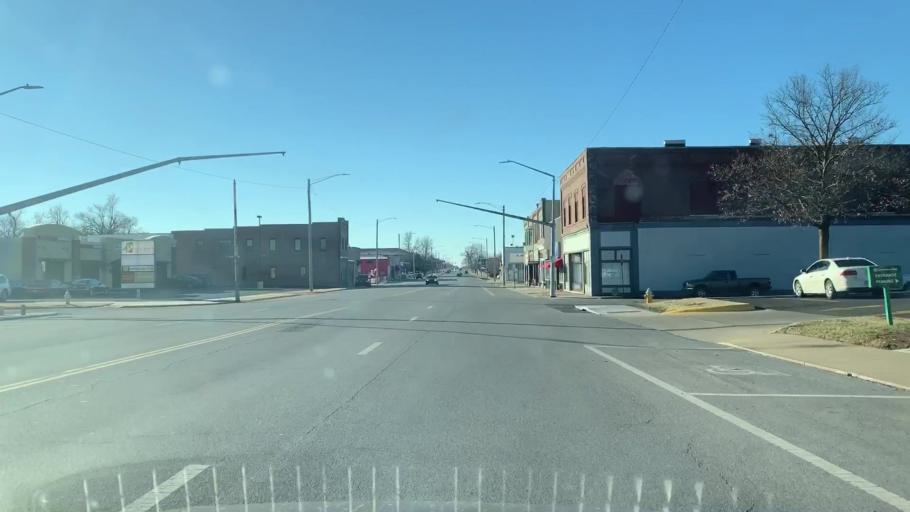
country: US
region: Kansas
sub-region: Crawford County
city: Pittsburg
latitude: 37.4077
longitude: -94.7049
